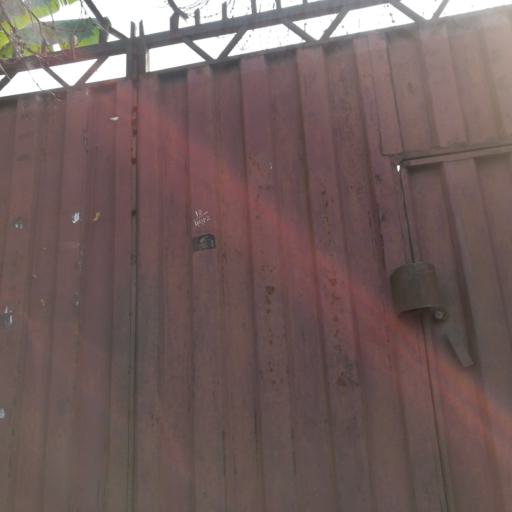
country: NG
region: Rivers
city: Port Harcourt
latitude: 4.8401
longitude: 7.0625
